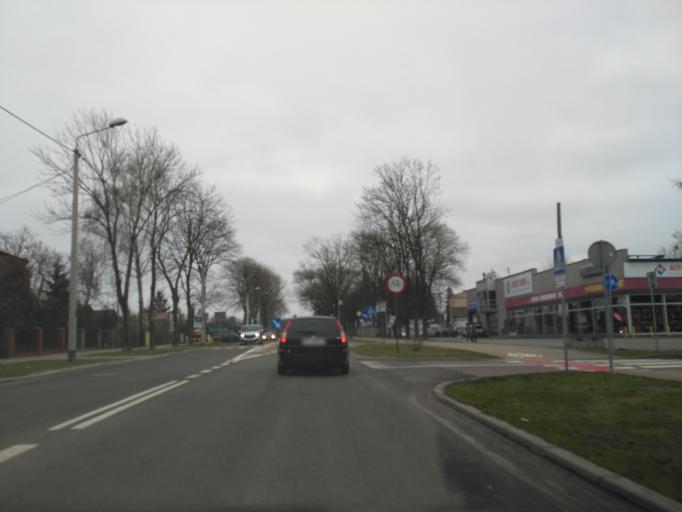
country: PL
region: Lublin Voivodeship
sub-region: Chelm
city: Chelm
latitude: 51.1249
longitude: 23.4956
